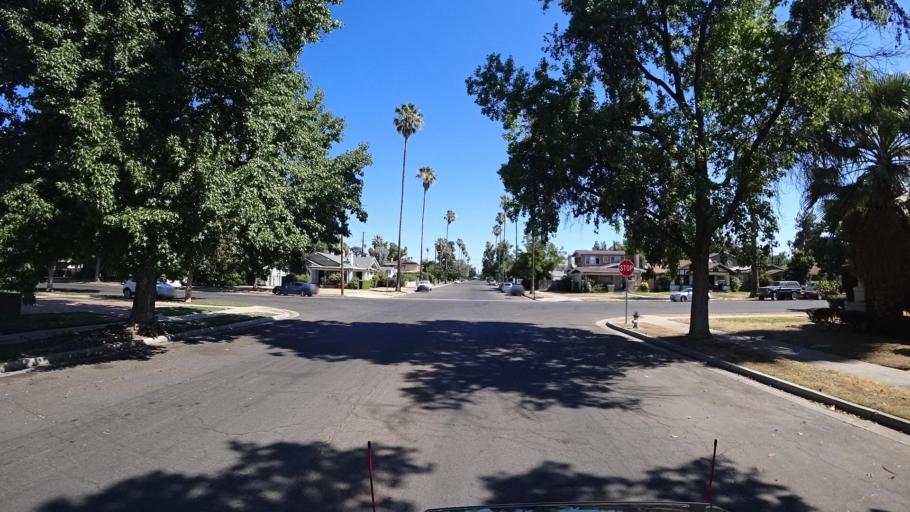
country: US
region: California
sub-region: Fresno County
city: Fresno
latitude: 36.7378
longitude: -119.7676
